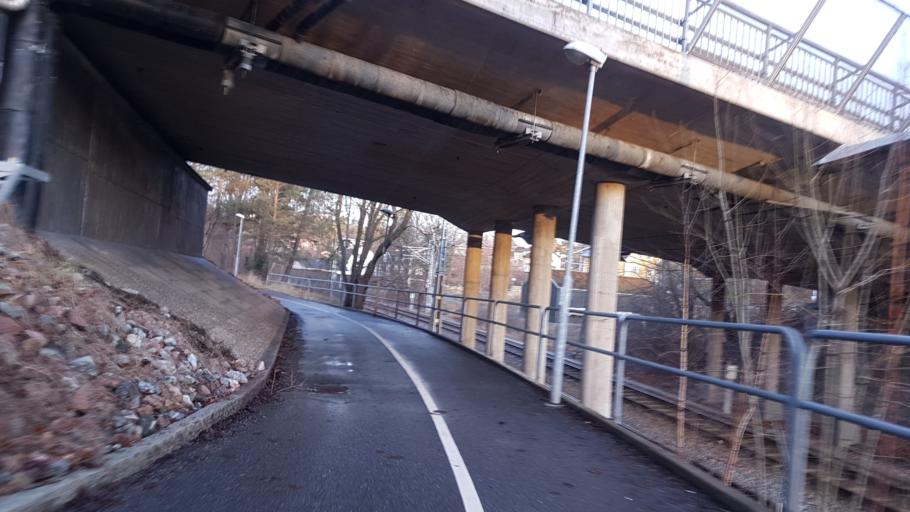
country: SE
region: Stockholm
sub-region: Lidingo
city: Lidingoe
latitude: 59.3559
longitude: 18.1359
